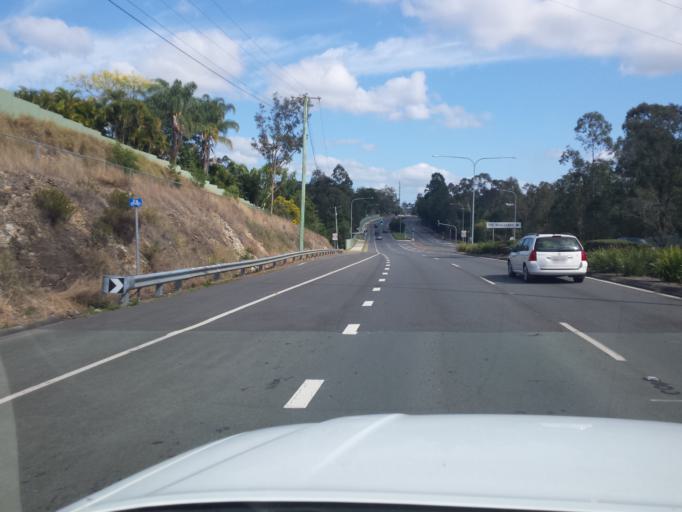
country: AU
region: Queensland
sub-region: Brisbane
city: Bridegman Downs
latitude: -27.3673
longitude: 152.9779
